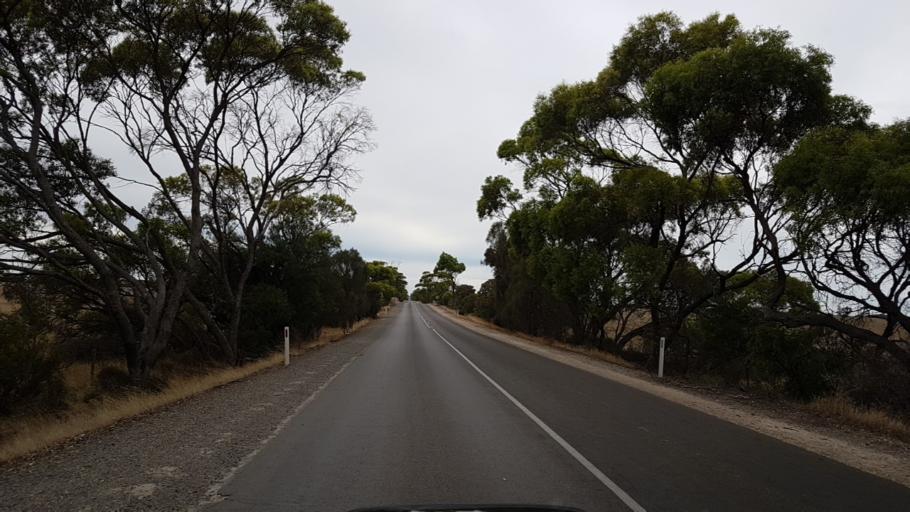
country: AU
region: South Australia
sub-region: Yorke Peninsula
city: Honiton
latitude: -34.9850
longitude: 137.2158
